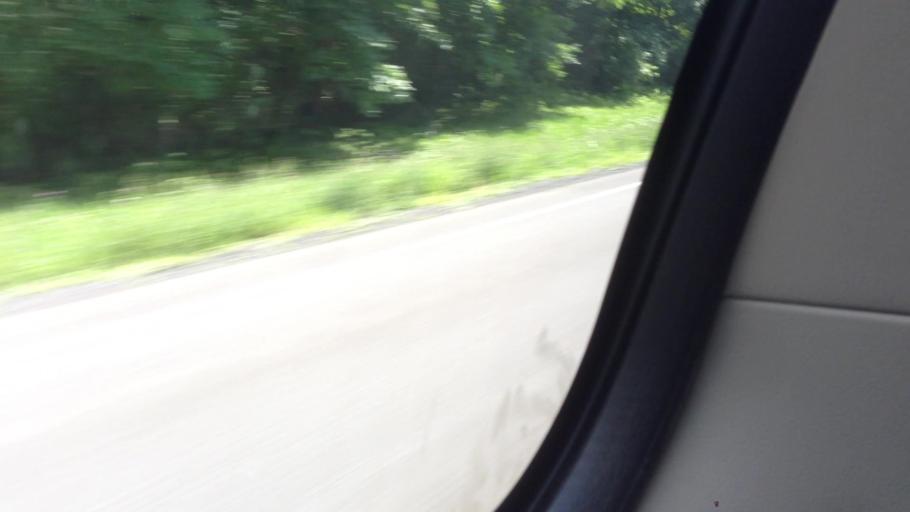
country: US
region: New York
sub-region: Dutchess County
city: Red Hook
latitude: 42.0153
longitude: -73.9060
